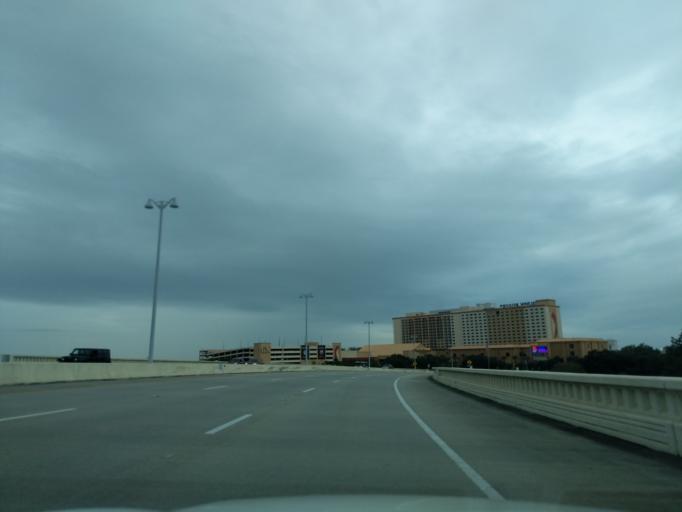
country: US
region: Mississippi
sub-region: Harrison County
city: Biloxi
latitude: 30.3947
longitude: -88.8575
